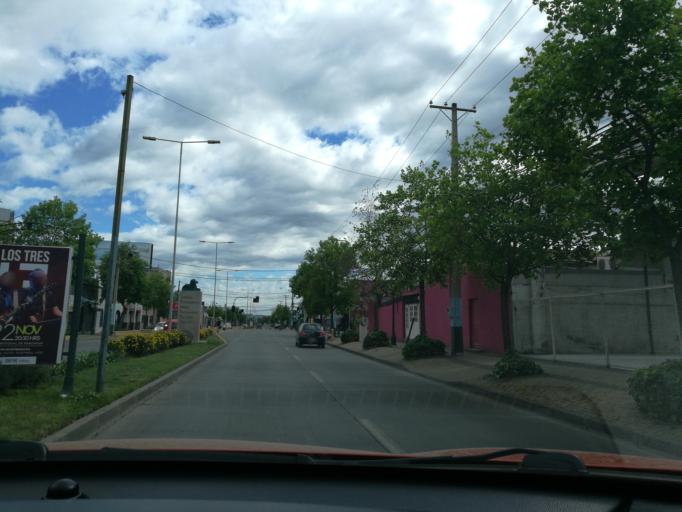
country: CL
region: O'Higgins
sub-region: Provincia de Cachapoal
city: Rancagua
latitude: -34.1700
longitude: -70.7348
